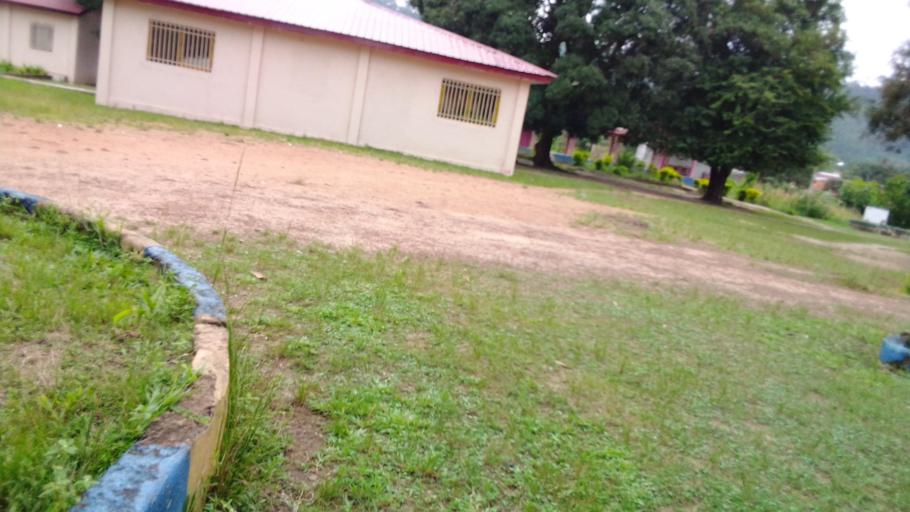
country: SL
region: Eastern Province
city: Kenema
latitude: 7.8624
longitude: -11.2023
